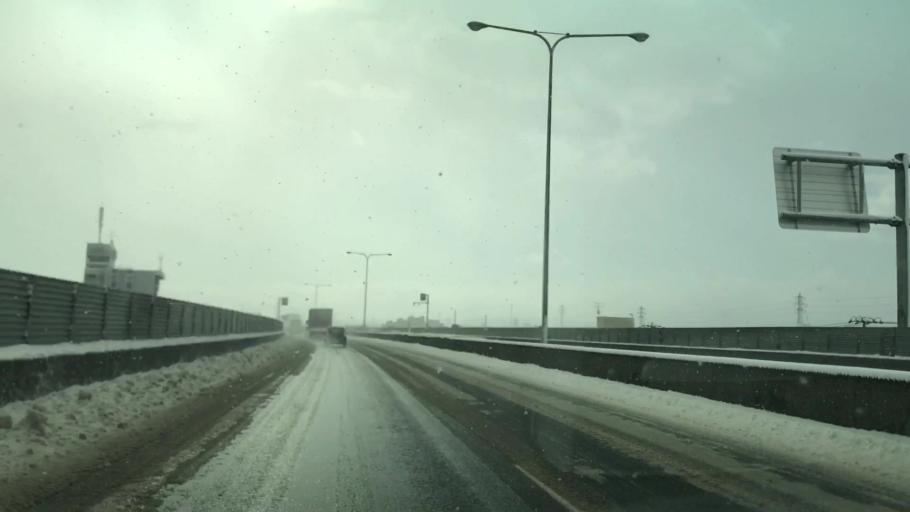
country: JP
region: Hokkaido
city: Sapporo
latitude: 43.0612
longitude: 141.4245
